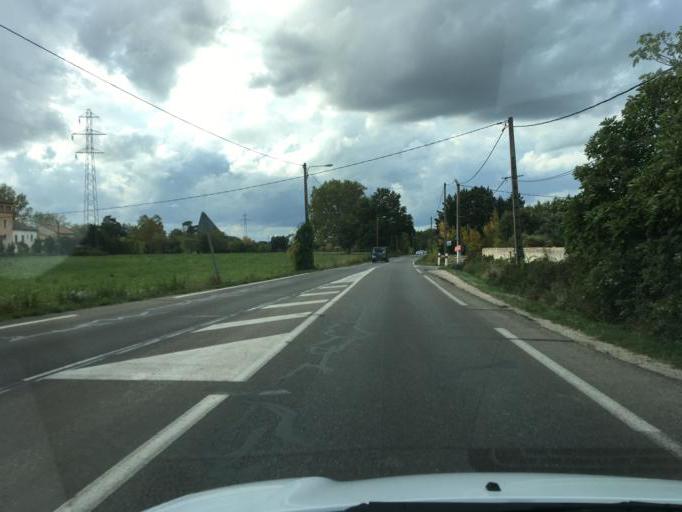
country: FR
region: Provence-Alpes-Cote d'Azur
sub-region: Departement du Vaucluse
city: Morieres-les-Avignon
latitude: 43.9421
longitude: 4.8897
